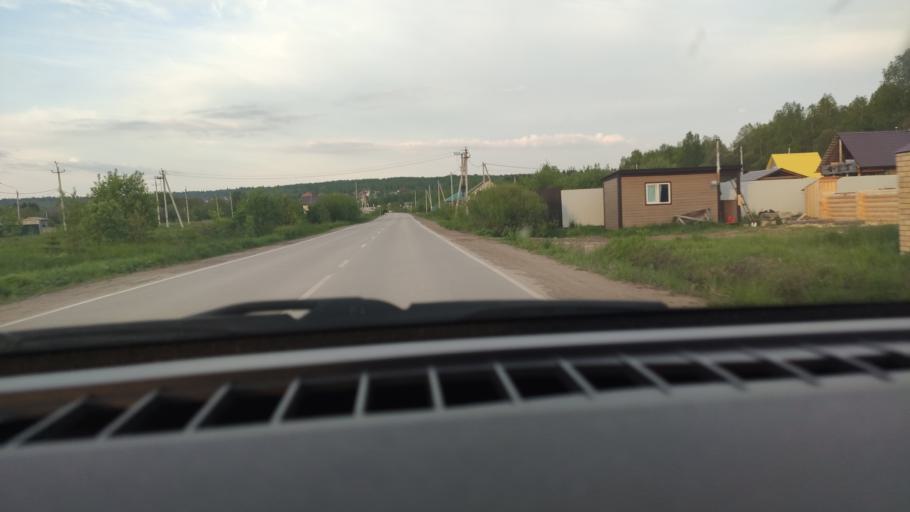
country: RU
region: Perm
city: Overyata
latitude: 58.0787
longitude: 55.9900
